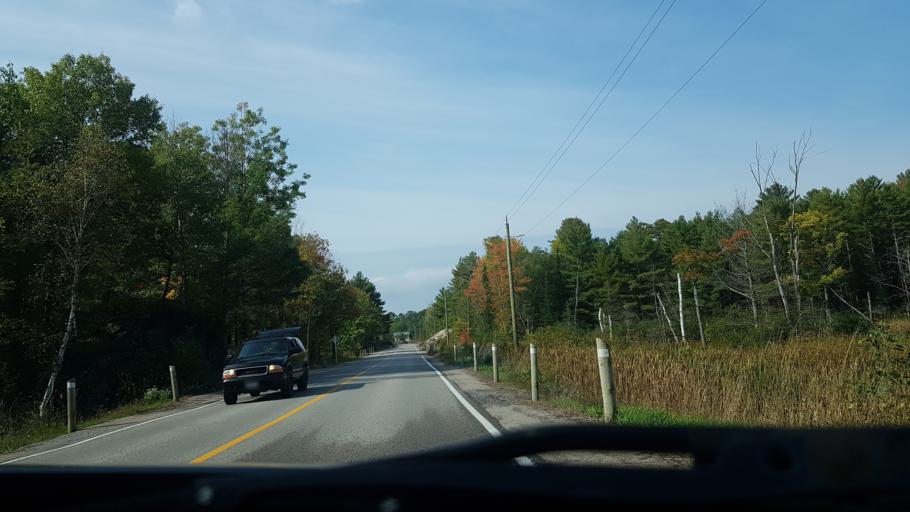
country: CA
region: Ontario
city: Gravenhurst
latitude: 44.7660
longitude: -79.3244
